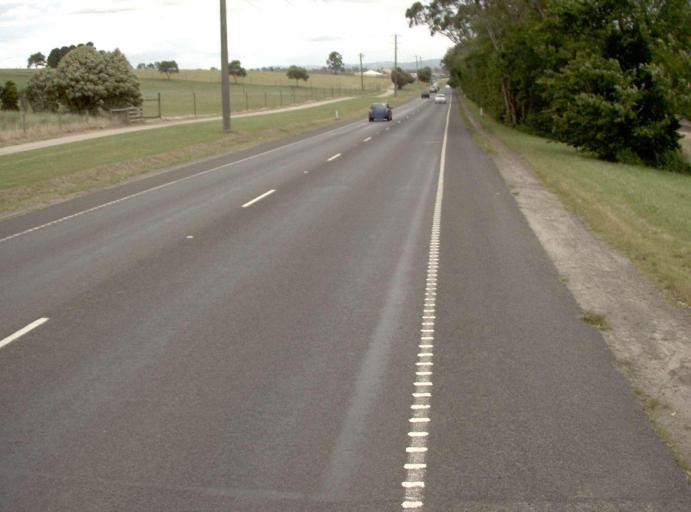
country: AU
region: Victoria
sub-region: Baw Baw
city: Warragul
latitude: -38.1467
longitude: 145.8984
